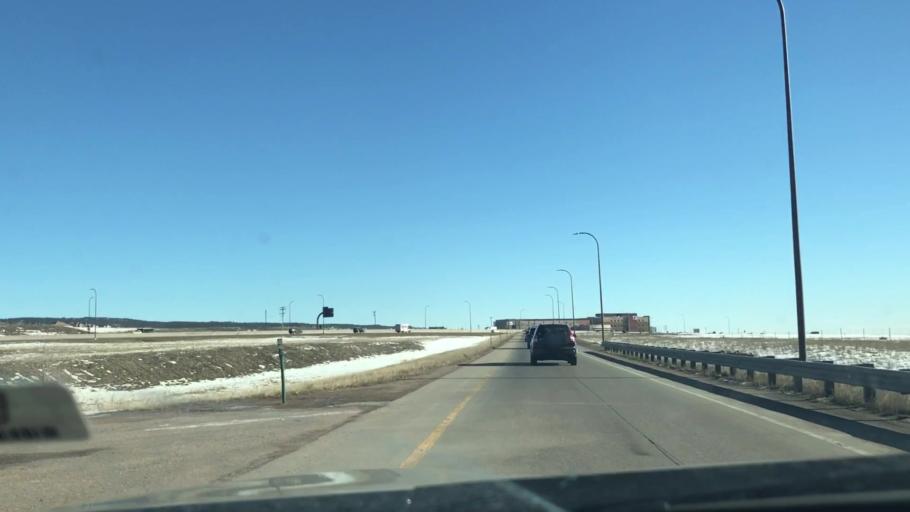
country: US
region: Colorado
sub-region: El Paso County
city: Monument
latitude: 39.0870
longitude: -104.8639
